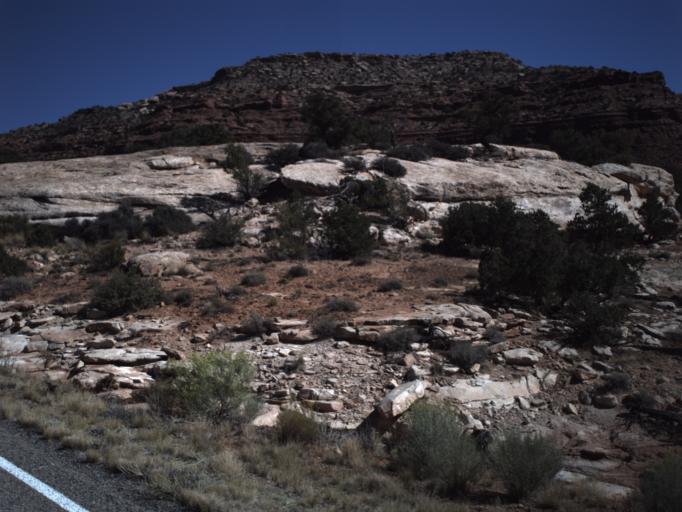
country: US
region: Utah
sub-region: San Juan County
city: Blanding
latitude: 37.6423
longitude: -110.1460
